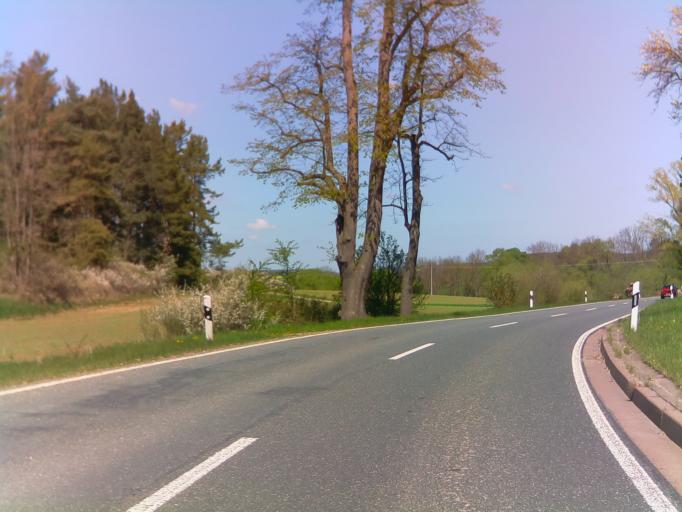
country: DE
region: Thuringia
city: Stadtilm
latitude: 50.7382
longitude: 11.0651
